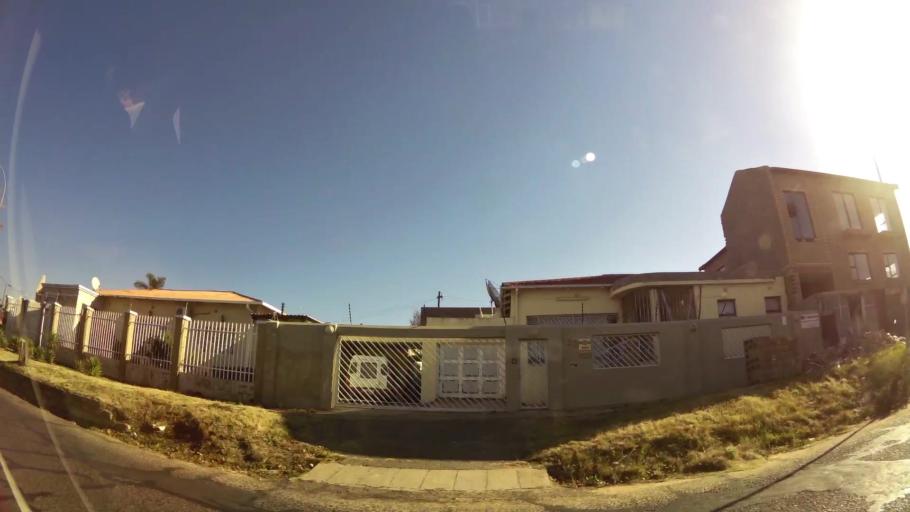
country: ZA
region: Gauteng
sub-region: City of Johannesburg Metropolitan Municipality
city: Johannesburg
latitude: -26.1998
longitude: 27.9992
